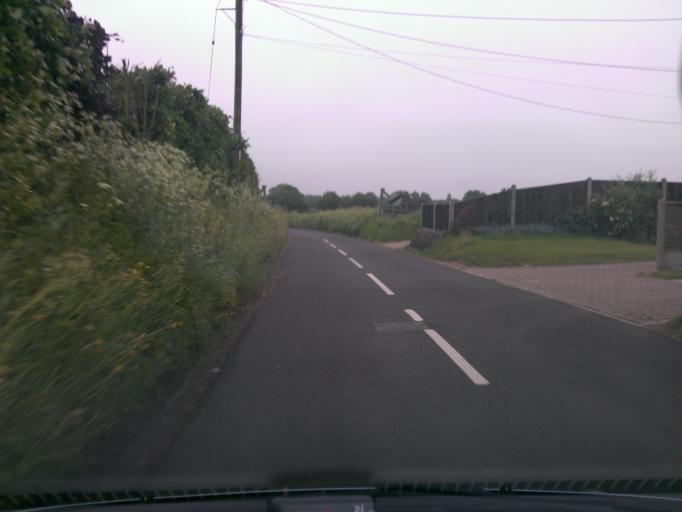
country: GB
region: England
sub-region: Essex
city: Marks Tey
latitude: 51.8506
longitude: 0.8037
